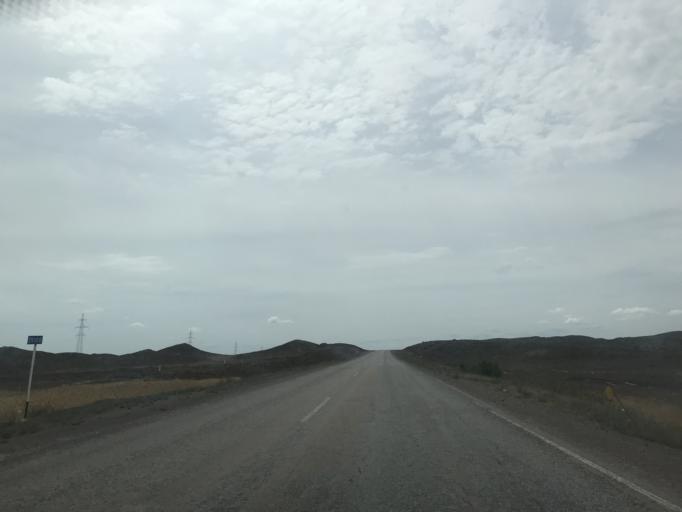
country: KZ
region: Zhambyl
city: Mynaral
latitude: 45.3882
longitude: 73.6482
